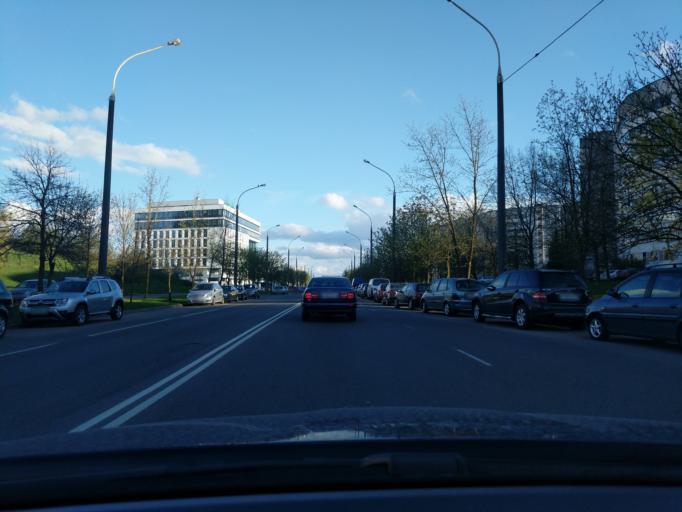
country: BY
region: Minsk
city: Novoye Medvezhino
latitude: 53.9110
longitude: 27.4515
